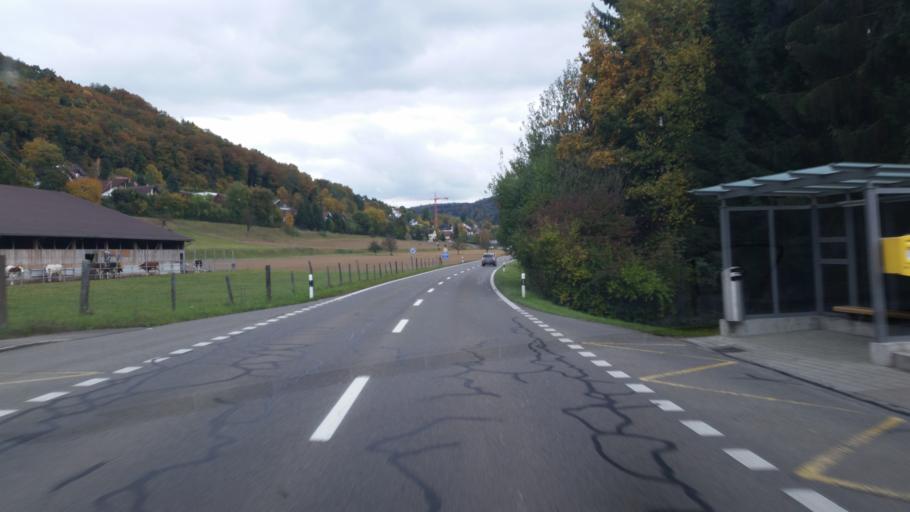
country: CH
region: Aargau
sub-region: Bezirk Zurzach
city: Oberendingen
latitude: 47.5465
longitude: 8.2895
